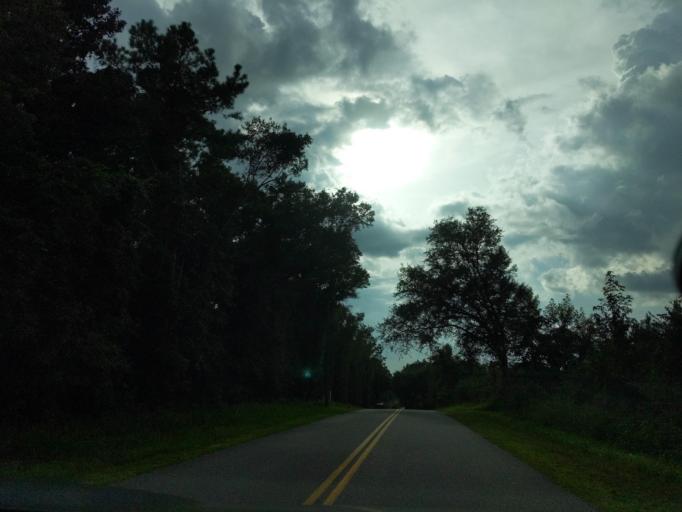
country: US
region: Florida
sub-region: Jefferson County
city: Monticello
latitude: 30.4782
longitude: -83.8911
